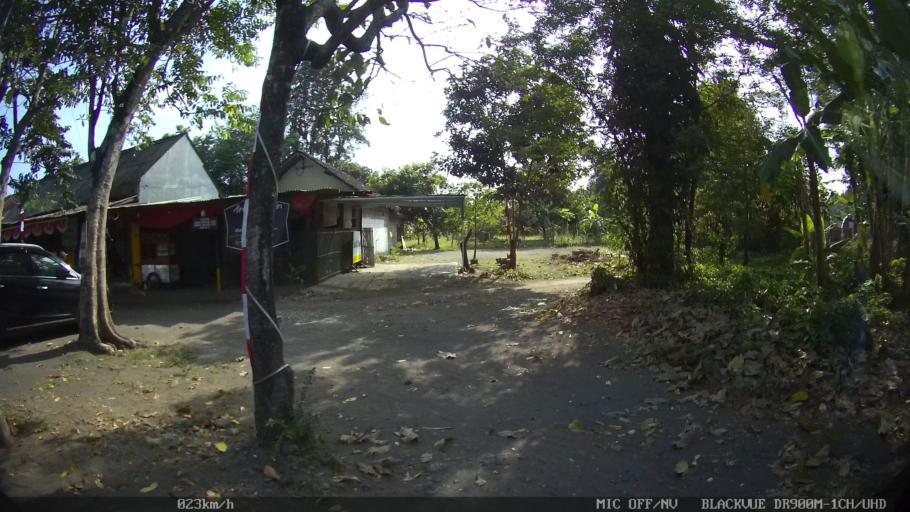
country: ID
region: Daerah Istimewa Yogyakarta
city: Kasihan
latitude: -7.8266
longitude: 110.3290
